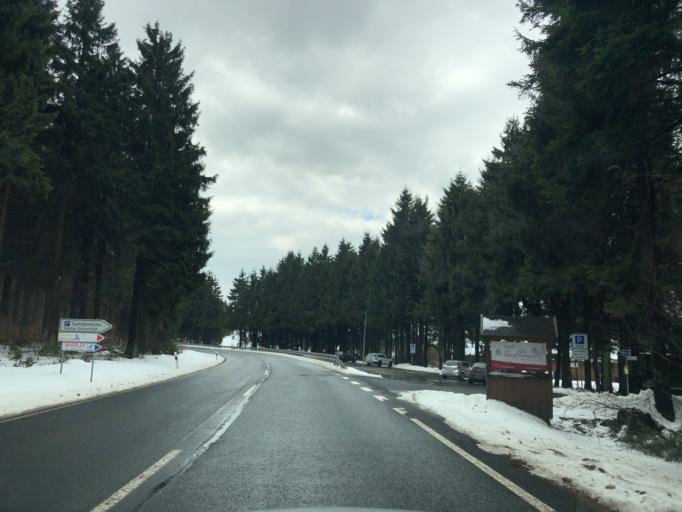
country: DE
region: Hesse
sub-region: Regierungsbezirk Giessen
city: Ulrichstein
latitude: 50.5171
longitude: 9.2294
